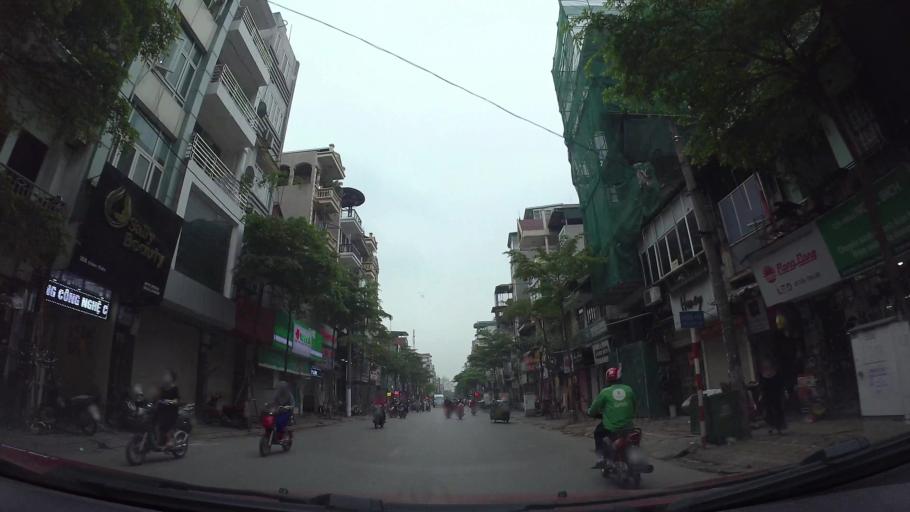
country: VN
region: Ha Noi
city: Dong Da
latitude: 21.0192
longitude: 105.8357
